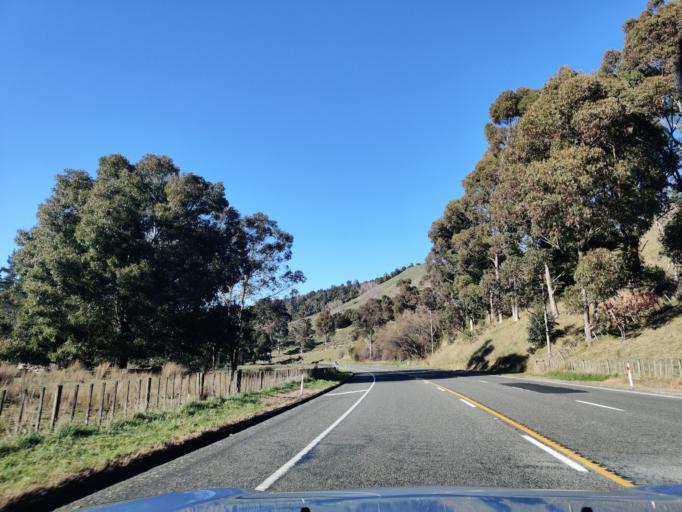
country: NZ
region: Manawatu-Wanganui
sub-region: Ruapehu District
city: Waiouru
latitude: -39.7934
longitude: 175.7854
